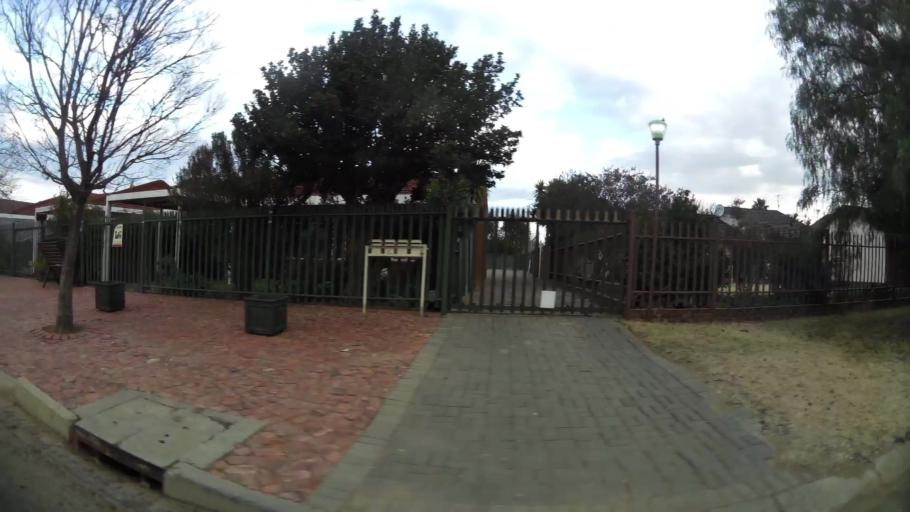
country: ZA
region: Orange Free State
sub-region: Lejweleputswa District Municipality
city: Welkom
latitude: -27.9783
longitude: 26.6996
